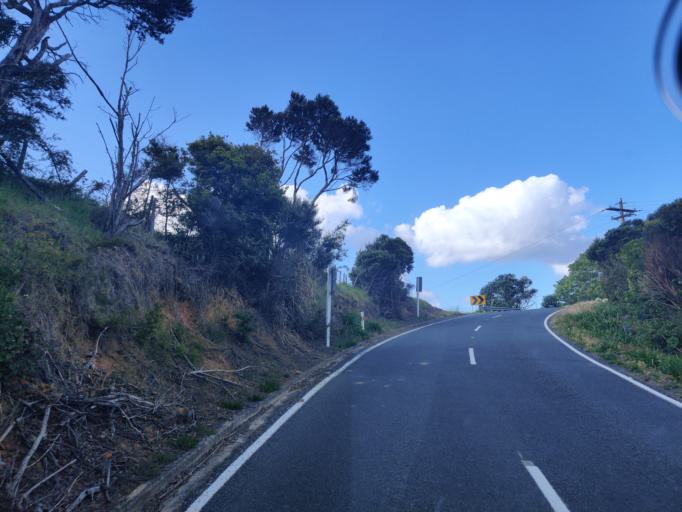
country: NZ
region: Northland
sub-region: Whangarei
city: Ngunguru
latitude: -35.6203
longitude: 174.5281
